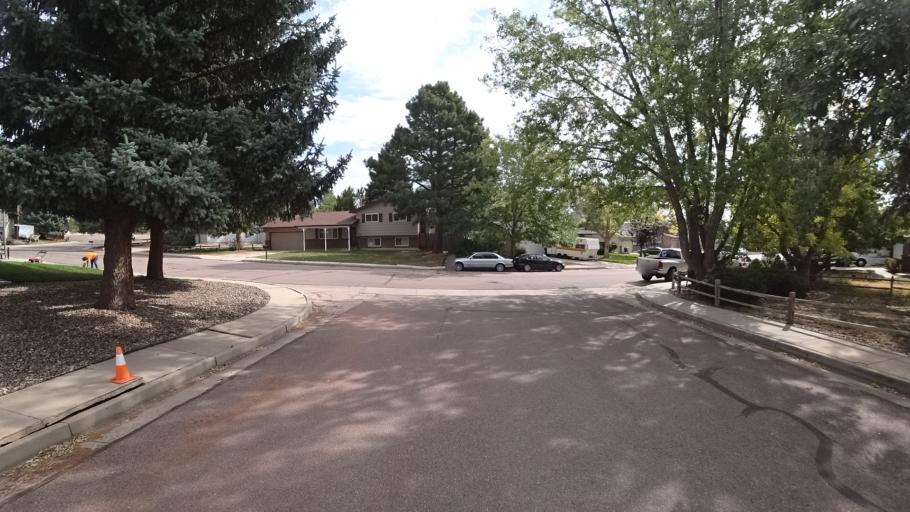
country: US
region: Colorado
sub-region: El Paso County
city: Cimarron Hills
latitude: 38.8483
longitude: -104.7262
